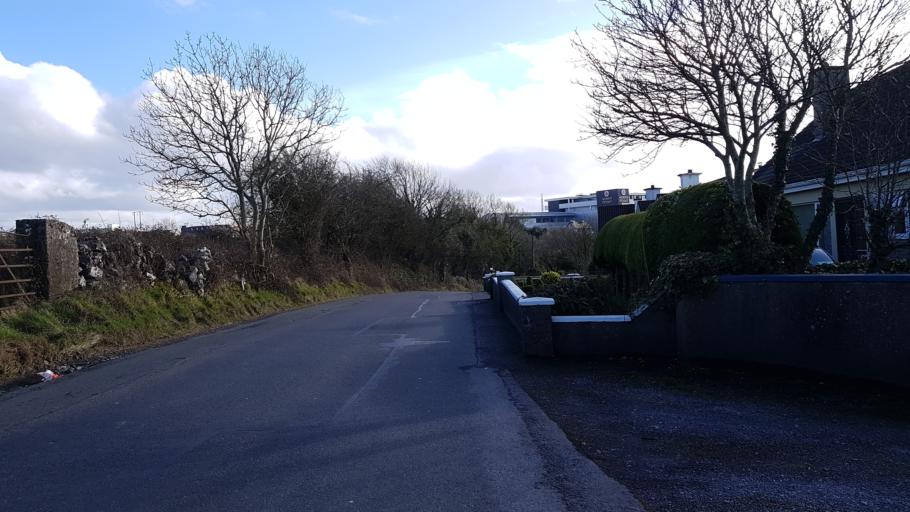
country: IE
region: Connaught
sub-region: County Galway
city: Gaillimh
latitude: 53.2975
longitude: -9.0168
